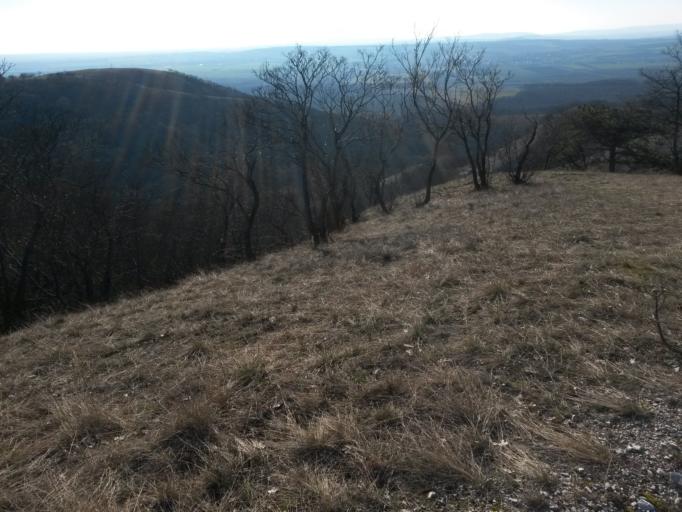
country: HU
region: Pest
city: Piliscsaba
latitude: 47.5962
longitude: 18.8221
